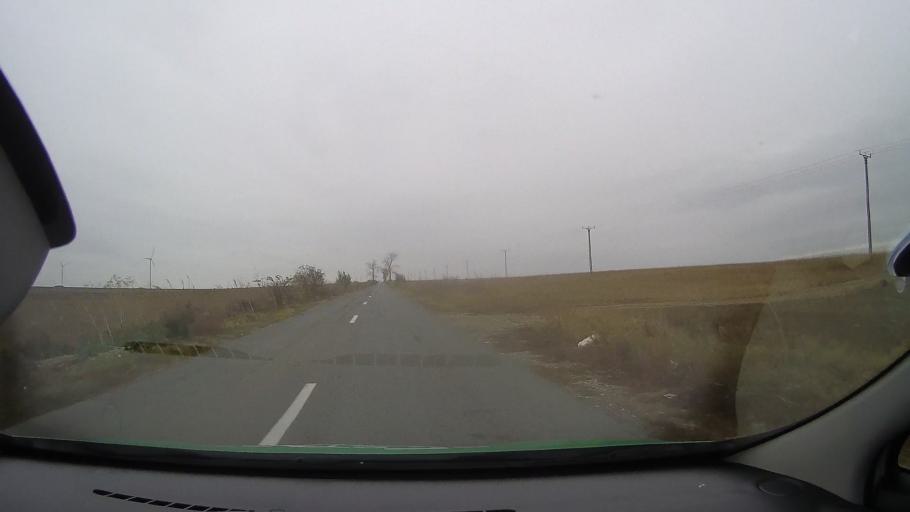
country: RO
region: Constanta
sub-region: Comuna Pantelimon
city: Pantelimon
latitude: 44.5634
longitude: 28.3200
